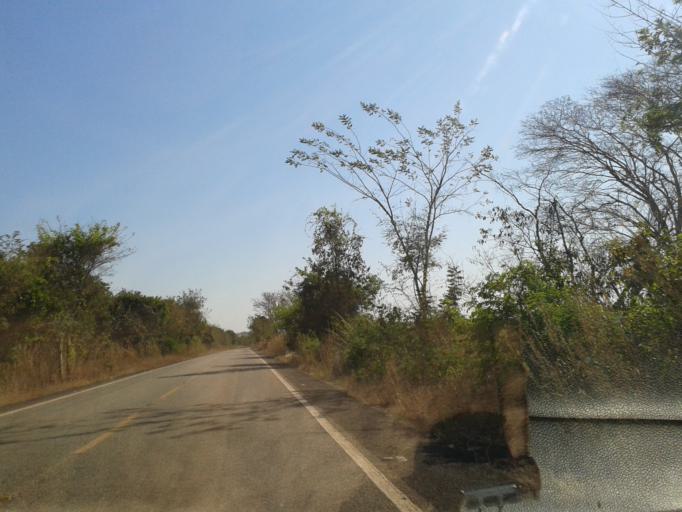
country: BR
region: Goias
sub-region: Mozarlandia
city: Mozarlandia
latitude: -14.6247
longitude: -50.5186
